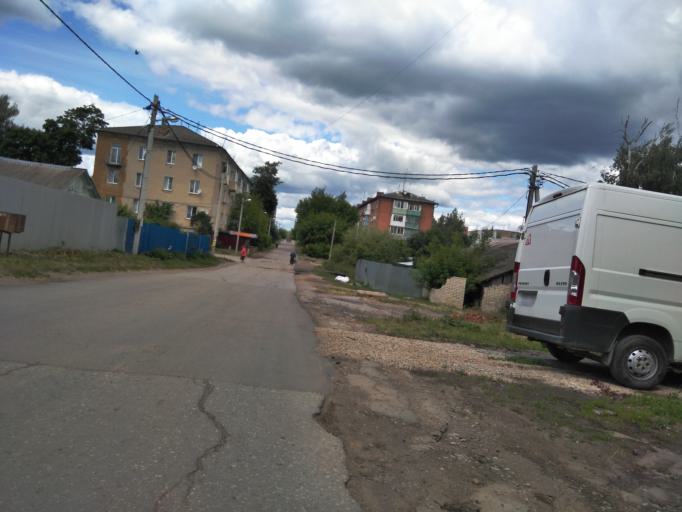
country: RU
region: Tula
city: Lomintsevskiy
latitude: 53.9357
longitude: 37.6301
